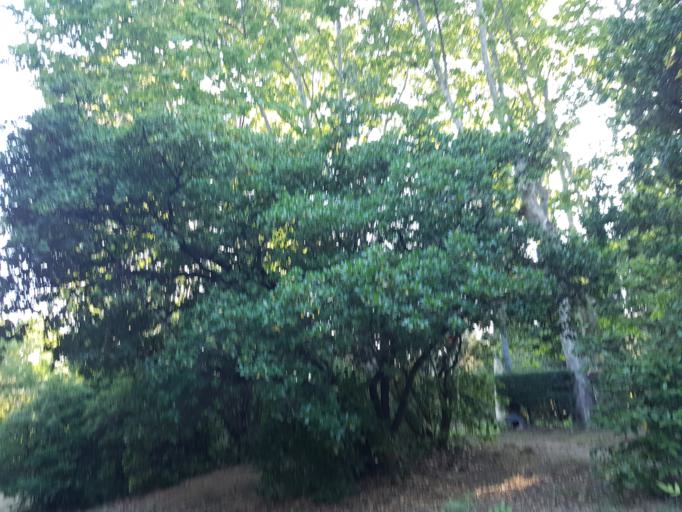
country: ES
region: Madrid
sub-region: Provincia de Madrid
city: Tetuan de las Victorias
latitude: 40.4496
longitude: -3.7211
